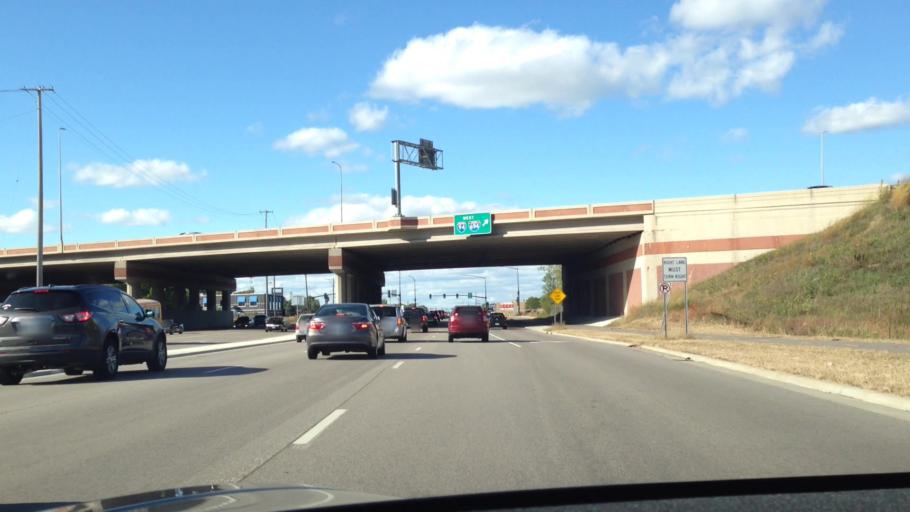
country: US
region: Minnesota
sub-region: Hennepin County
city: Brooklyn Park
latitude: 45.0772
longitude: -93.3729
